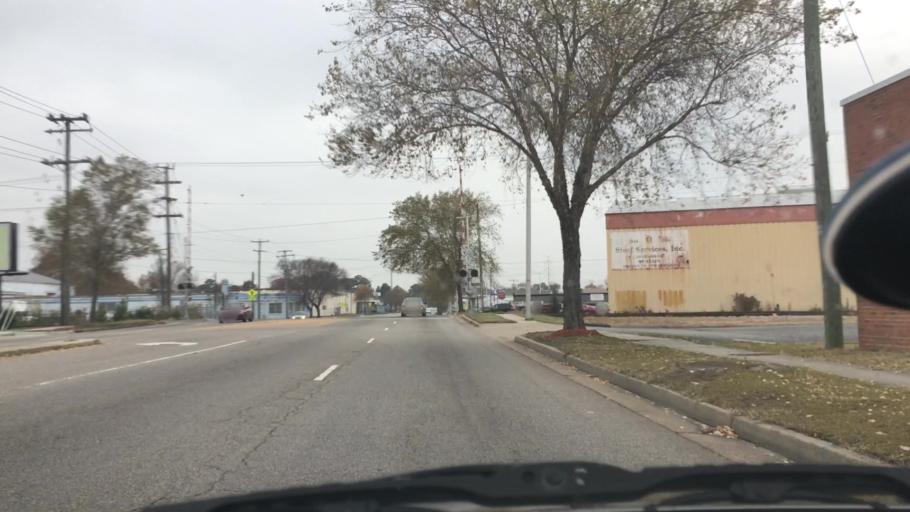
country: US
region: Virginia
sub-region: City of Norfolk
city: Norfolk
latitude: 36.8641
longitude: -76.2451
